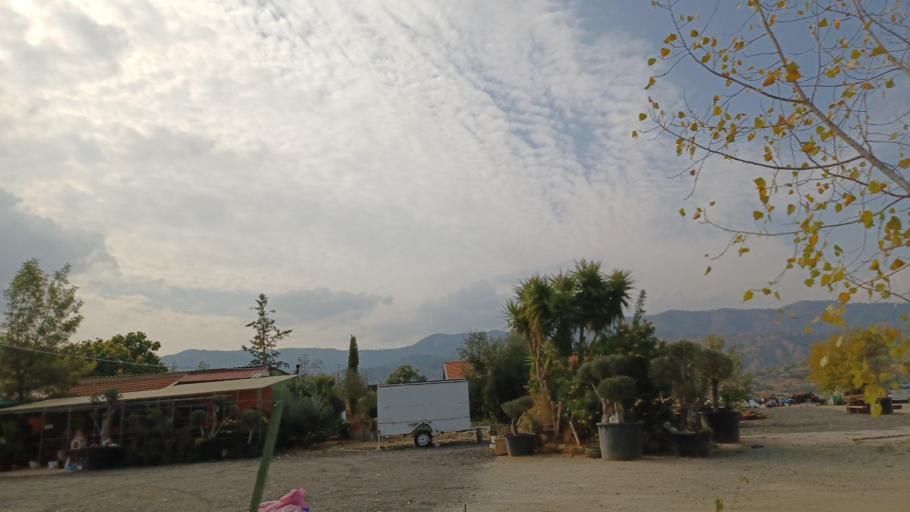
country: CY
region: Lefkosia
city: Kakopetria
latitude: 35.0290
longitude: 32.9009
